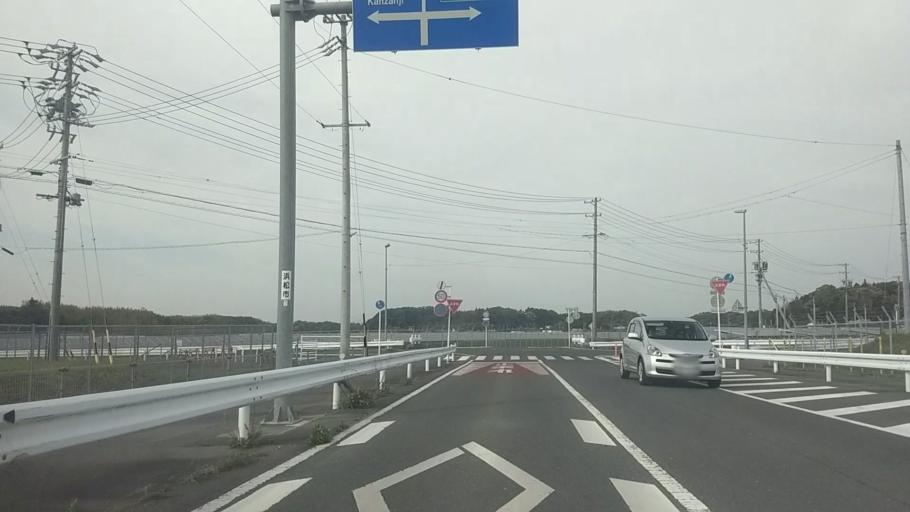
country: JP
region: Shizuoka
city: Kosai-shi
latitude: 34.7394
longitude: 137.6097
